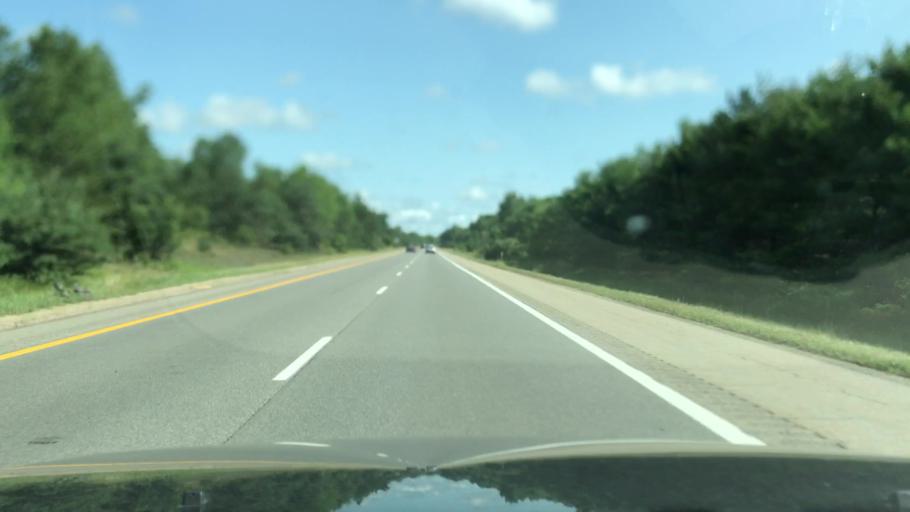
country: US
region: Michigan
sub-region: Kent County
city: Cedar Springs
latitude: 43.2400
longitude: -85.5608
